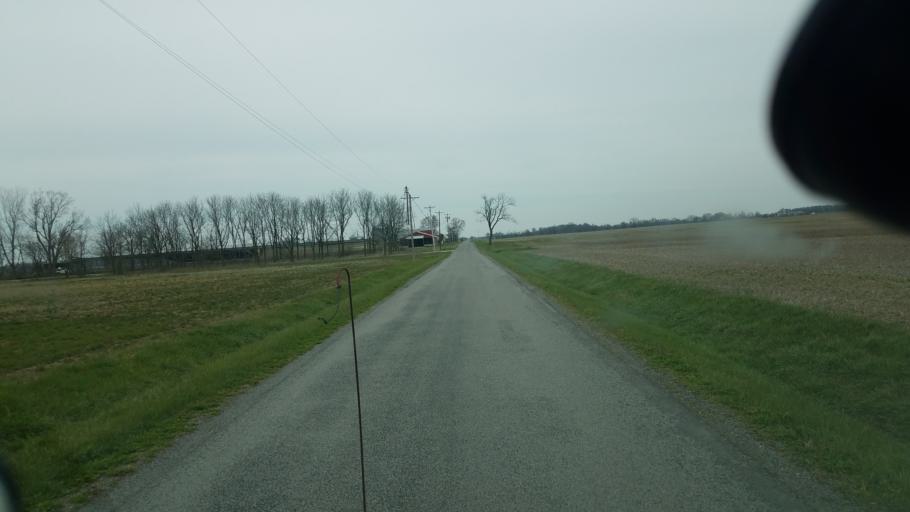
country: US
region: Ohio
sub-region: Hardin County
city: Forest
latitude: 40.9109
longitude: -83.5146
